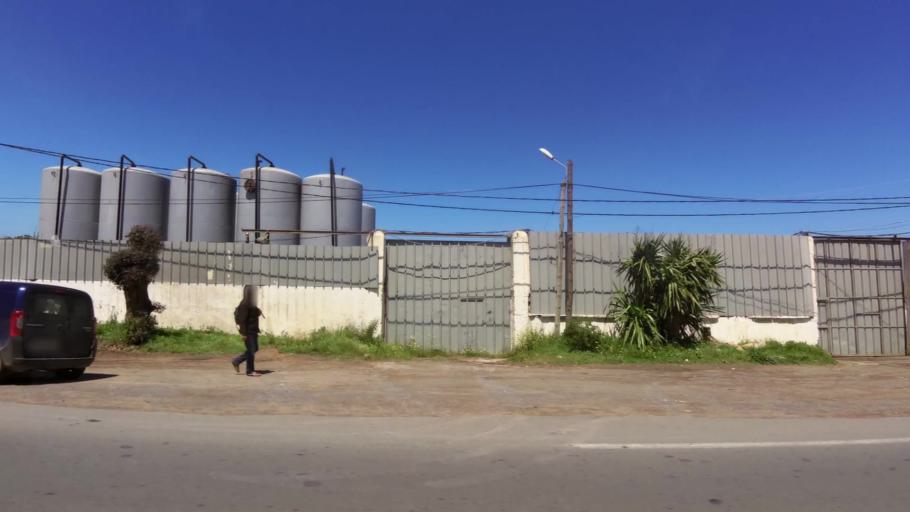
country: MA
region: Grand Casablanca
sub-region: Nouaceur
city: Dar Bouazza
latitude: 33.5167
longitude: -7.8054
